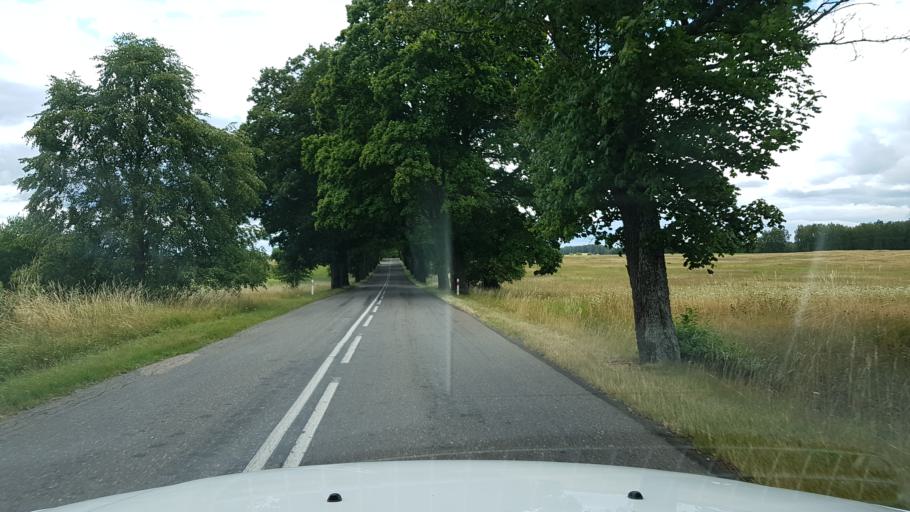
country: PL
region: West Pomeranian Voivodeship
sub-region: Powiat stargardzki
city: Insko
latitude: 53.3857
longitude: 15.5770
